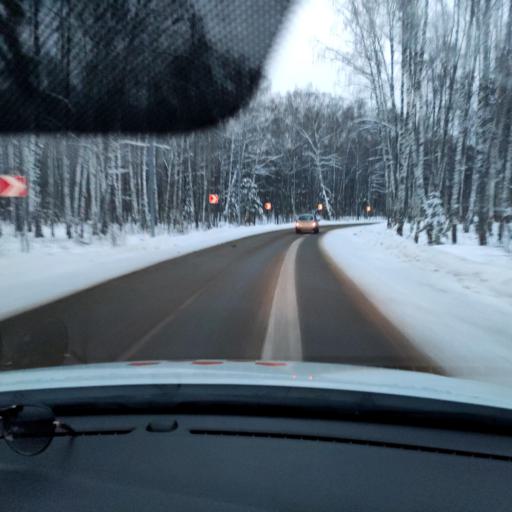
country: RU
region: Tatarstan
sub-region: Gorod Kazan'
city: Kazan
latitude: 55.9308
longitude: 49.1564
